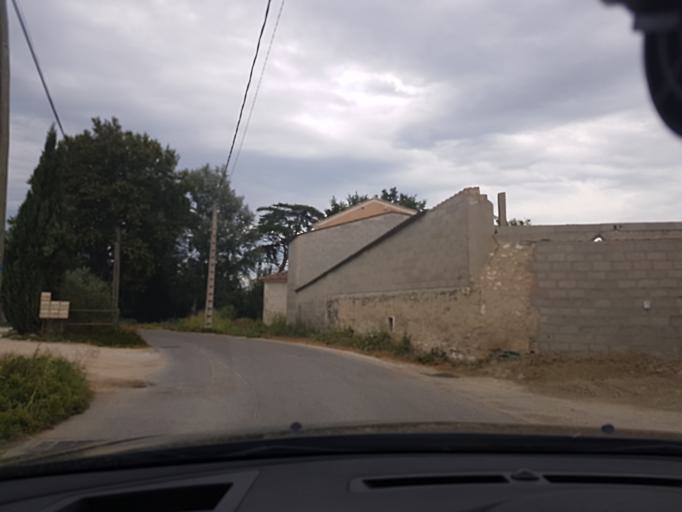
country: FR
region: Provence-Alpes-Cote d'Azur
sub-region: Departement du Vaucluse
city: Jonquerettes
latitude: 43.9504
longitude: 4.9429
